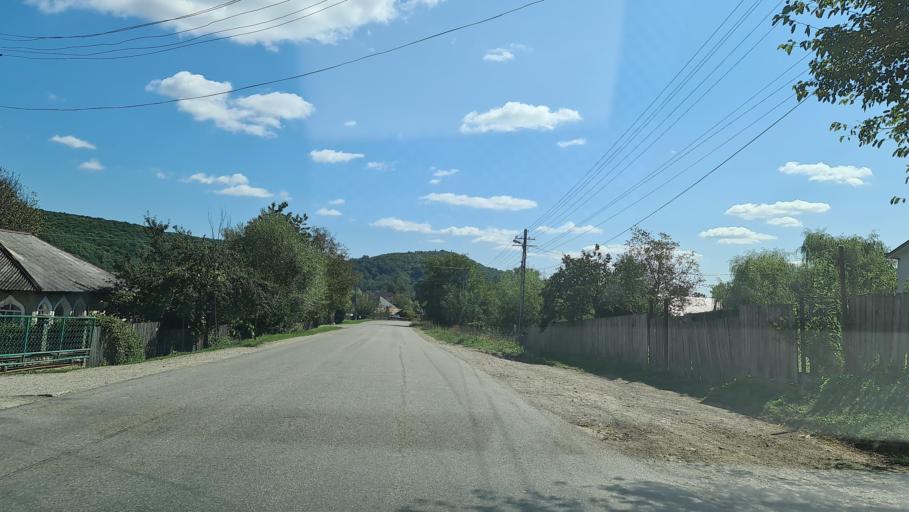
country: RO
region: Bacau
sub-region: Comuna Scorteni
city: Scorteni
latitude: 46.5237
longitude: 26.6654
